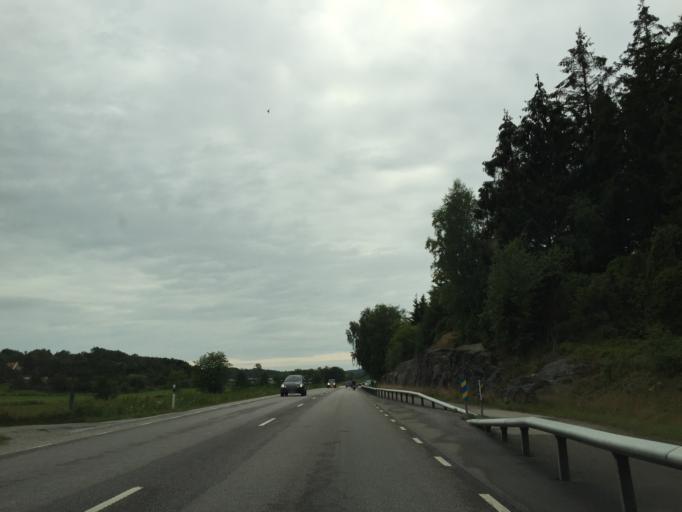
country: SE
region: Vaestra Goetaland
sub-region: Tjorns Kommun
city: Myggenas
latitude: 58.0364
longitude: 11.7301
